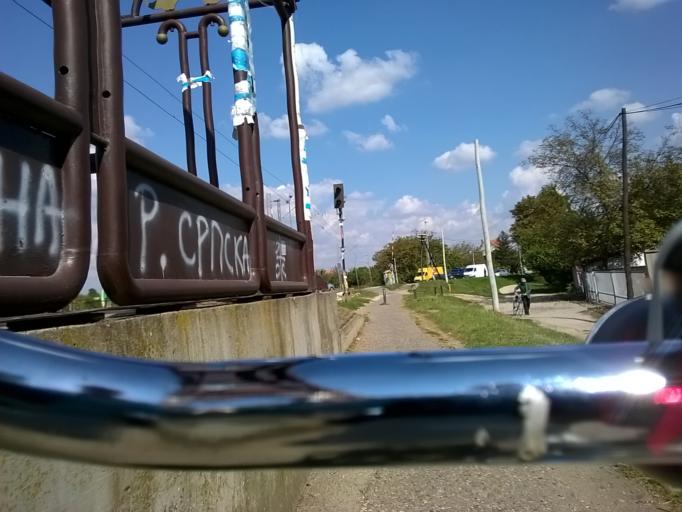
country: RS
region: Autonomna Pokrajina Vojvodina
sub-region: Juznobanatski Okrug
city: Pancevo
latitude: 44.8701
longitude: 20.6665
